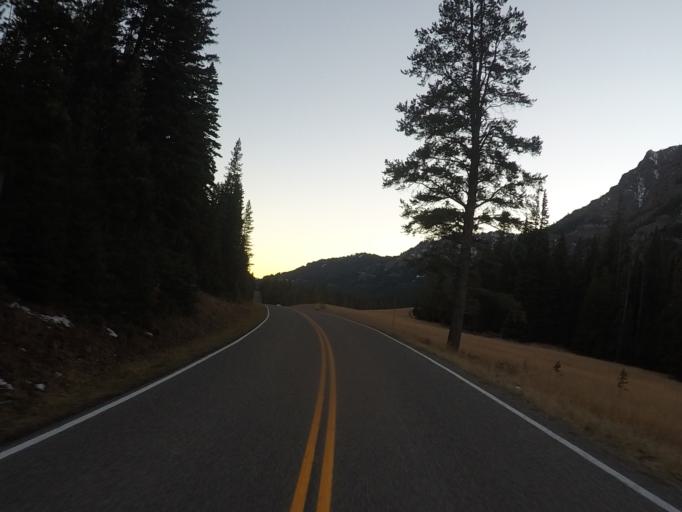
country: US
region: Montana
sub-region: Stillwater County
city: Absarokee
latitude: 44.9811
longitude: -110.0616
